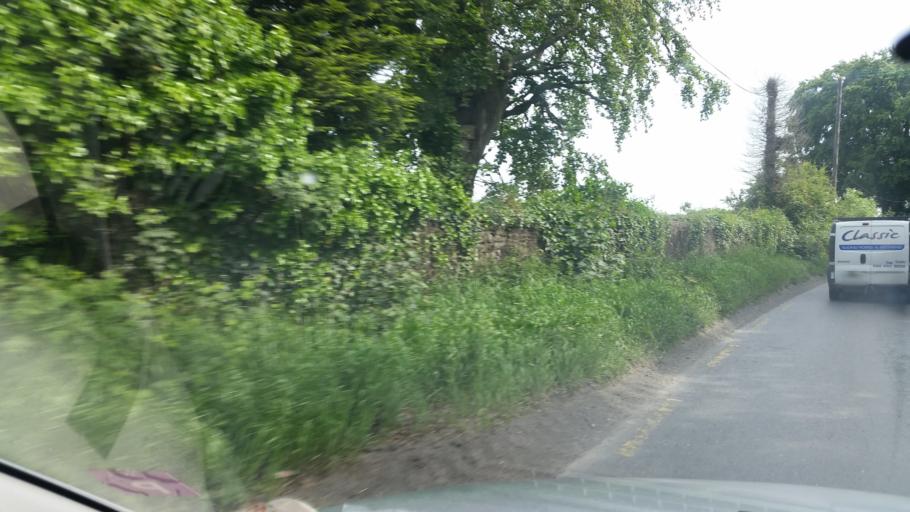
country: IE
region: Leinster
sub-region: Fingal County
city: Swords
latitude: 53.4500
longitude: -6.2606
